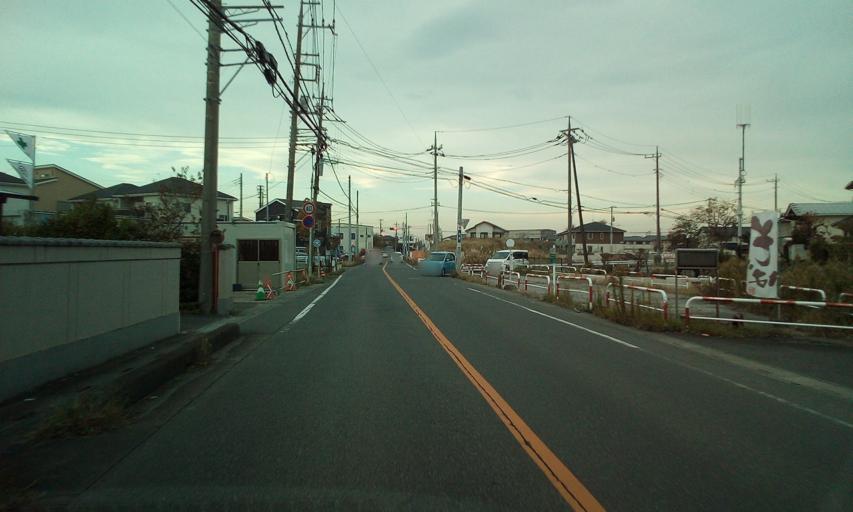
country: JP
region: Saitama
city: Yashio-shi
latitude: 35.8463
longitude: 139.8609
